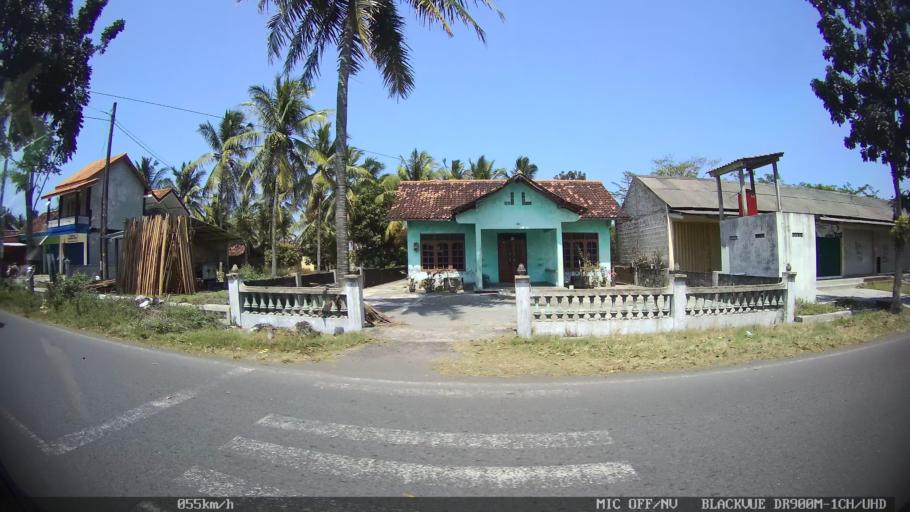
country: ID
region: Daerah Istimewa Yogyakarta
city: Srandakan
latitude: -7.9137
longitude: 110.0949
